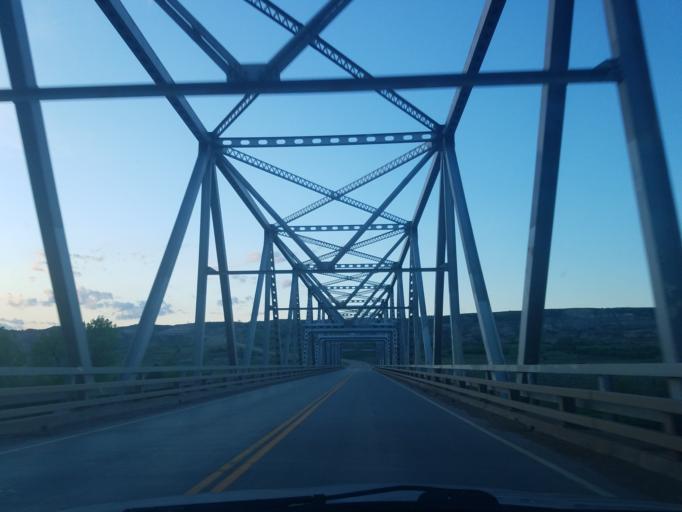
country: US
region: North Dakota
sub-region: McKenzie County
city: Watford City
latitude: 47.5903
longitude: -103.2532
